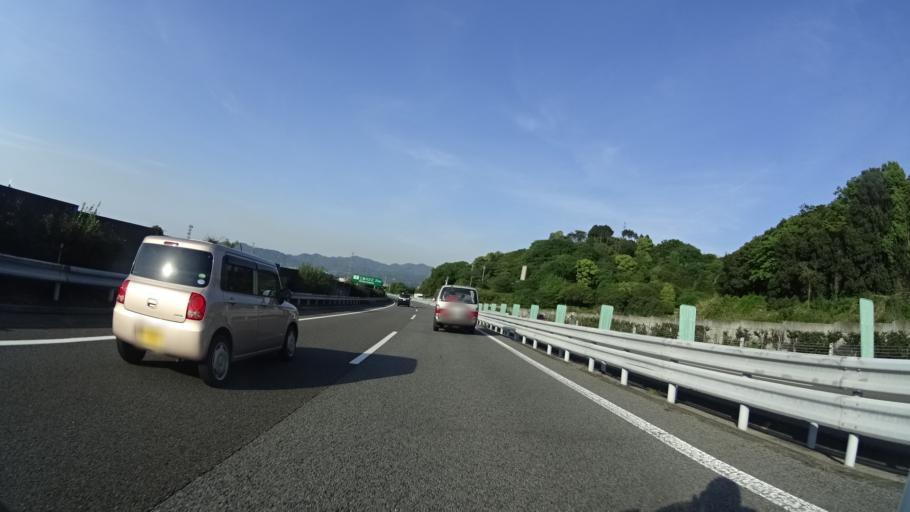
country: JP
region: Ehime
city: Kawanoecho
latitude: 33.9707
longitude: 133.5545
